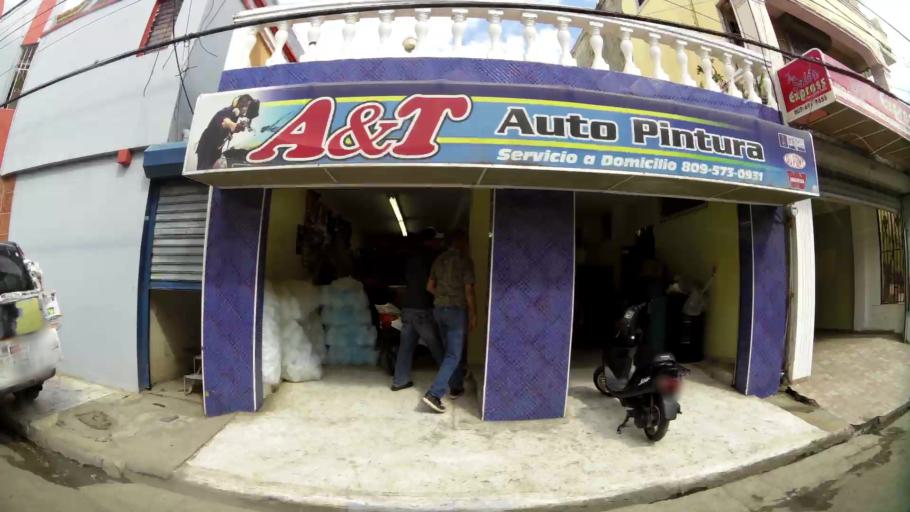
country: DO
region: La Vega
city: Concepcion de La Vega
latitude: 19.2271
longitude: -70.5333
